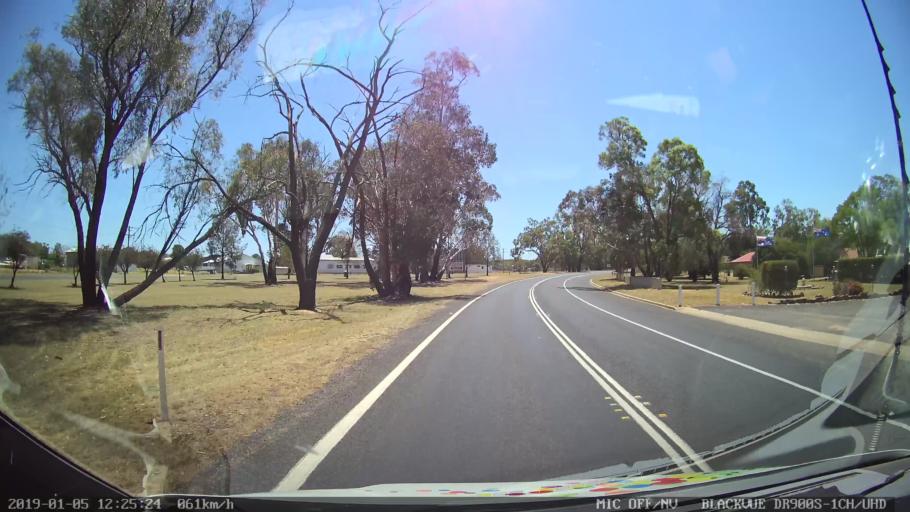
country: AU
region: New South Wales
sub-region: Warrumbungle Shire
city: Coonabarabran
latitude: -31.2607
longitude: 149.2849
